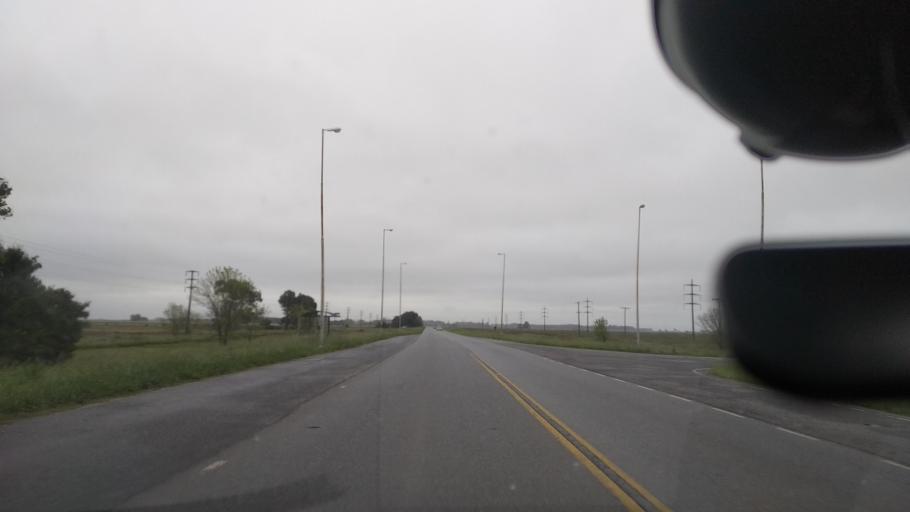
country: AR
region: Buenos Aires
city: Veronica
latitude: -35.3627
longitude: -57.3983
